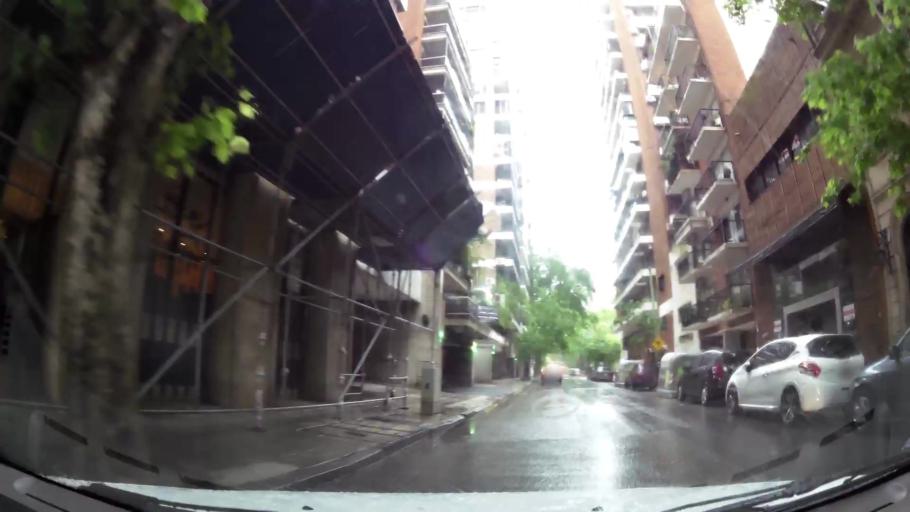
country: AR
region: Buenos Aires F.D.
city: Retiro
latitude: -34.5761
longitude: -58.4064
